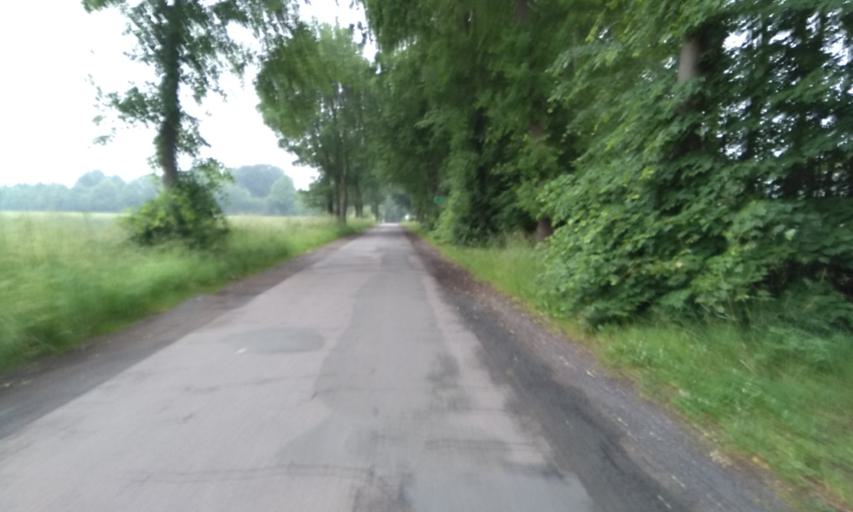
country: DE
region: Lower Saxony
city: Deinste
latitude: 53.5418
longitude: 9.4323
